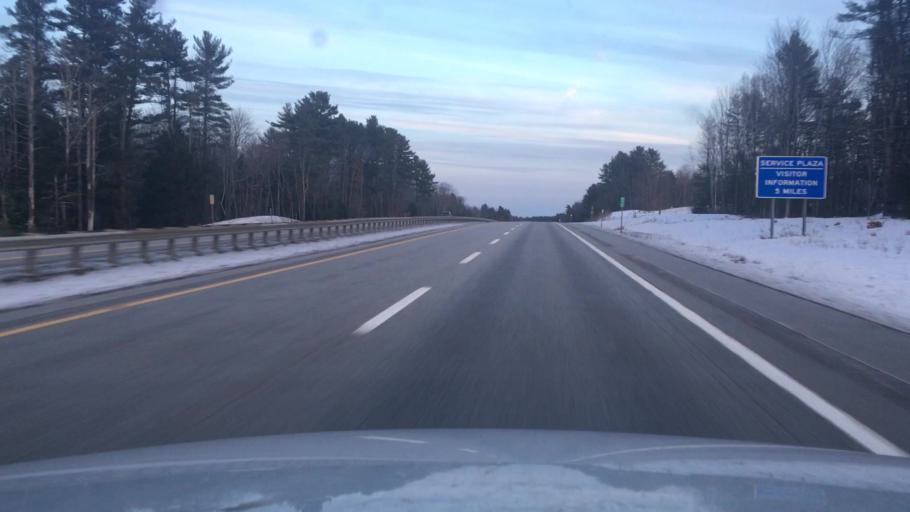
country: US
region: Maine
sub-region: Sagadahoc County
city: Richmond
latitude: 44.1583
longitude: -69.8937
